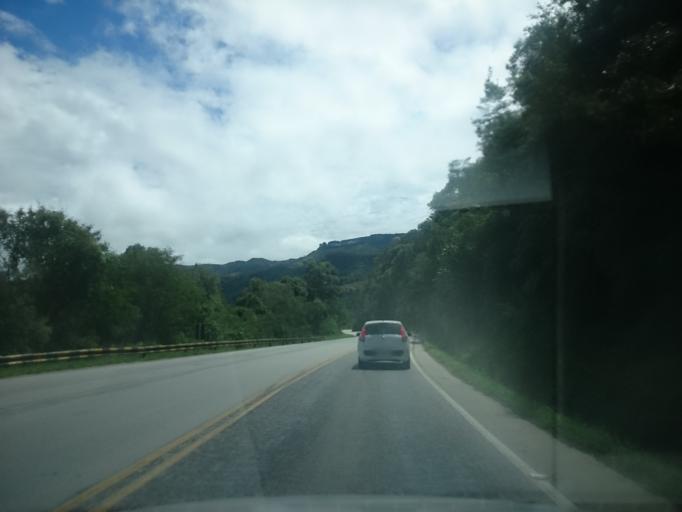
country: BR
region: Santa Catarina
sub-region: Anitapolis
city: Anitapolis
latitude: -27.6672
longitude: -49.1922
